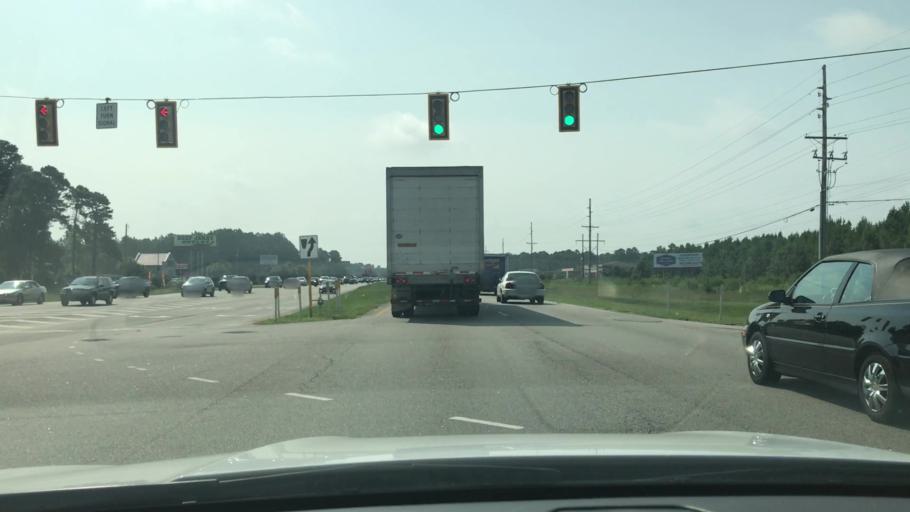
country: US
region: South Carolina
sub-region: Horry County
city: Red Hill
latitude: 33.7823
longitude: -78.9895
